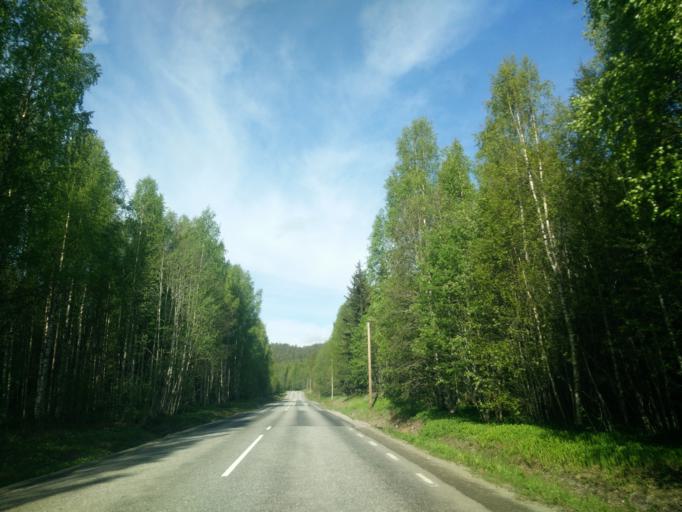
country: SE
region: Vaesternorrland
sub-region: Sundsvalls Kommun
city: Sundsvall
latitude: 62.3046
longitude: 17.2797
